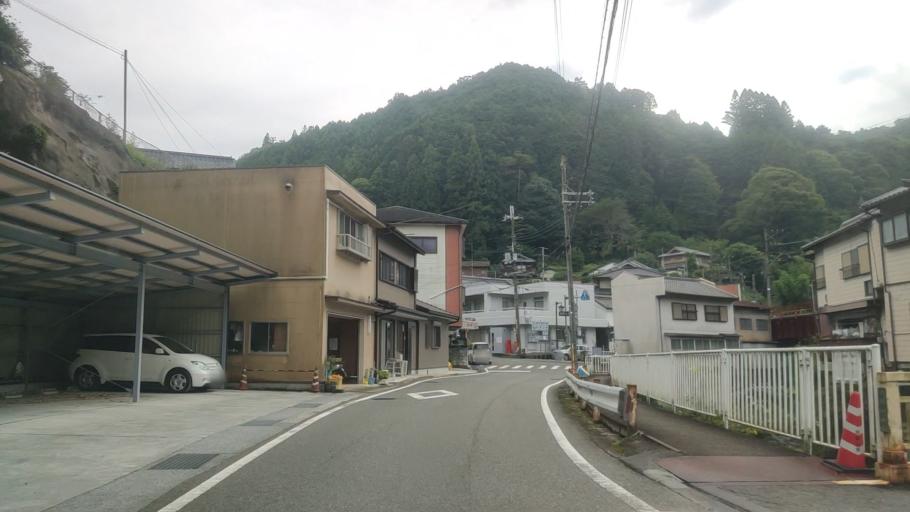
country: JP
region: Wakayama
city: Hashimoto
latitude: 34.2713
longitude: 135.5665
